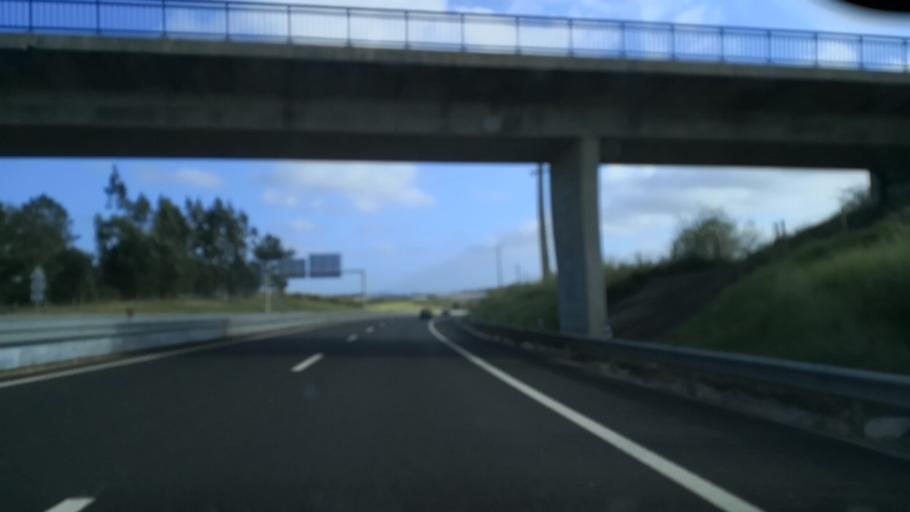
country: PT
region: Leiria
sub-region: Bombarral
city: Bombarral
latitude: 39.2553
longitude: -9.1647
